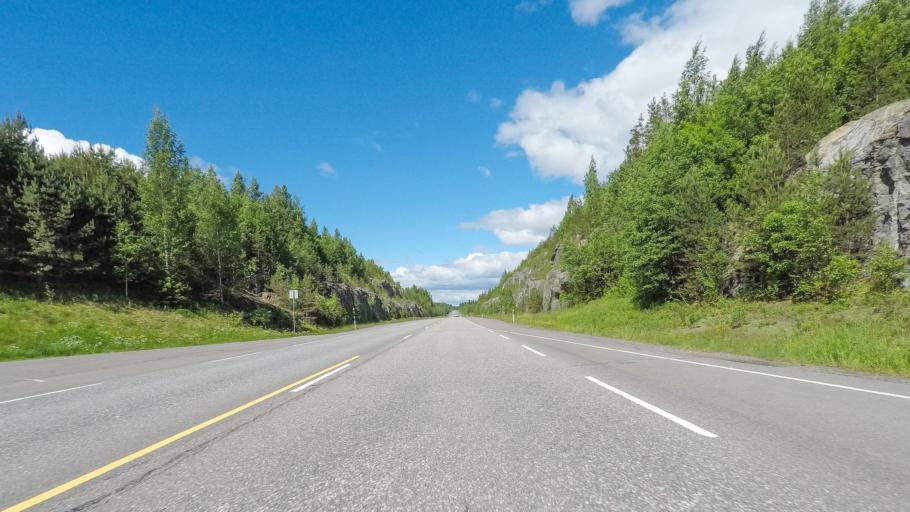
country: FI
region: Paijanne Tavastia
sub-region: Lahti
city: Heinola
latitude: 61.3135
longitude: 26.0441
